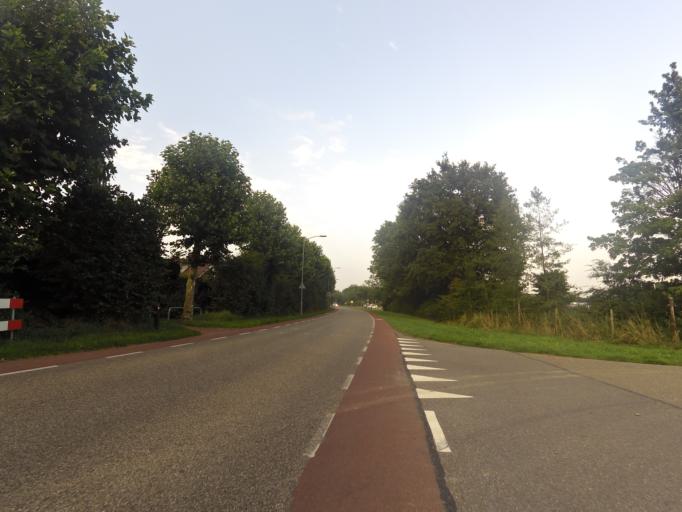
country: NL
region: Gelderland
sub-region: Oude IJsselstreek
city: Gendringen
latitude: 51.8822
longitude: 6.3770
